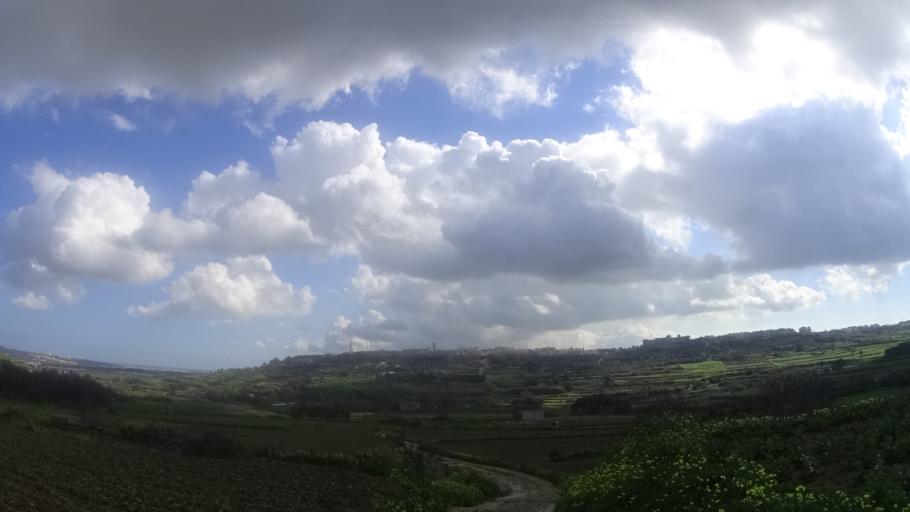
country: MT
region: L-Imtarfa
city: Imtarfa
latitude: 35.8984
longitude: 14.3875
